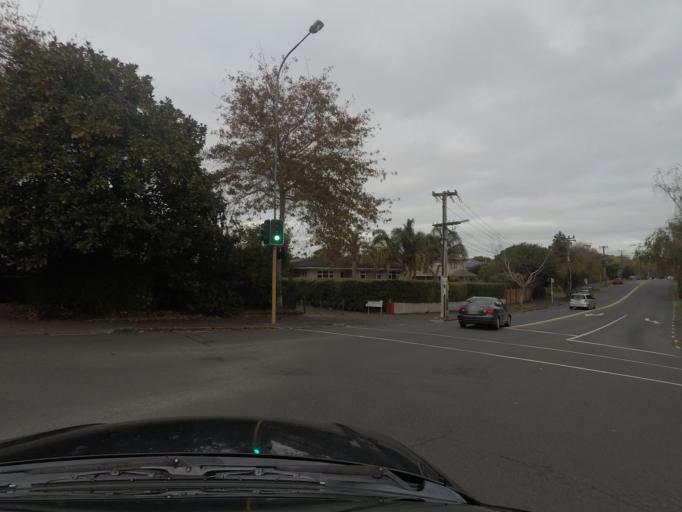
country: NZ
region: Auckland
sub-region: Auckland
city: Auckland
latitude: -36.8888
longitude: 174.7702
